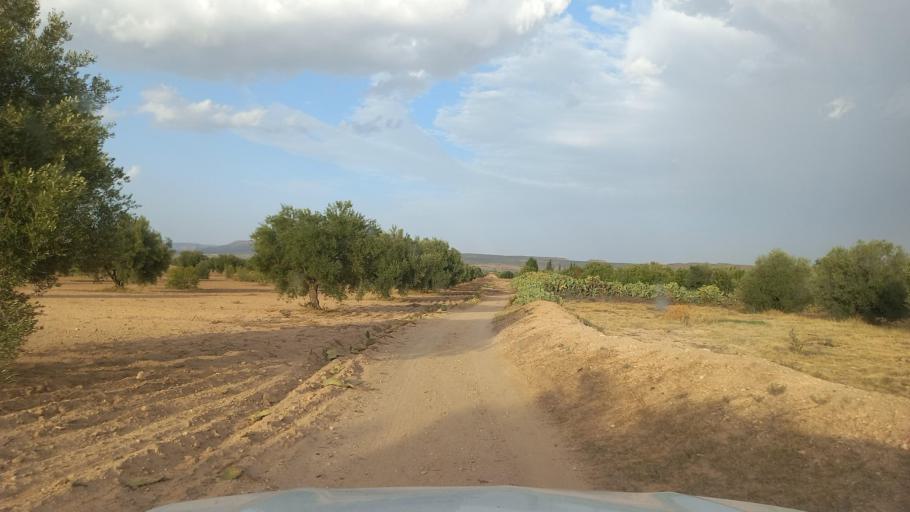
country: TN
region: Al Qasrayn
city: Sbiba
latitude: 35.2852
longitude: 9.0719
